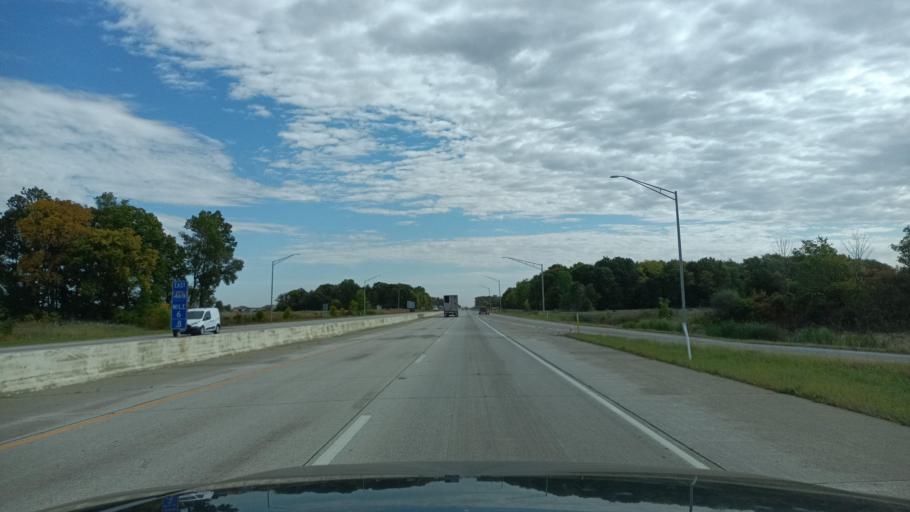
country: US
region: Indiana
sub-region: Wells County
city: Ossian
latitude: 40.9545
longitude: -85.1648
